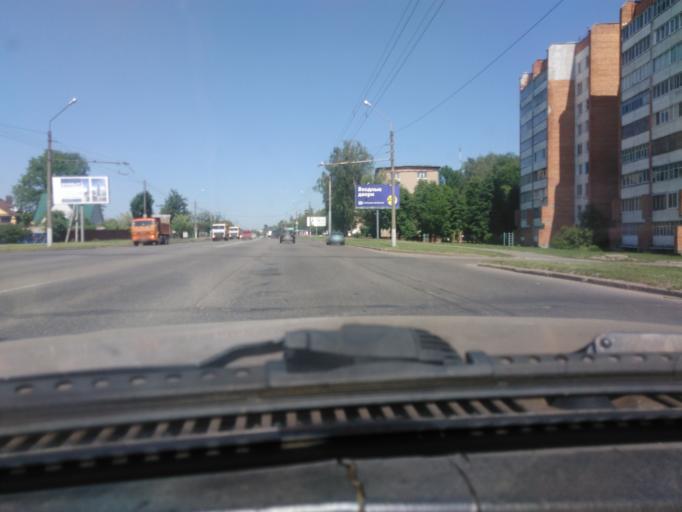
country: BY
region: Mogilev
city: Mahilyow
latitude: 53.9352
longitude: 30.3531
